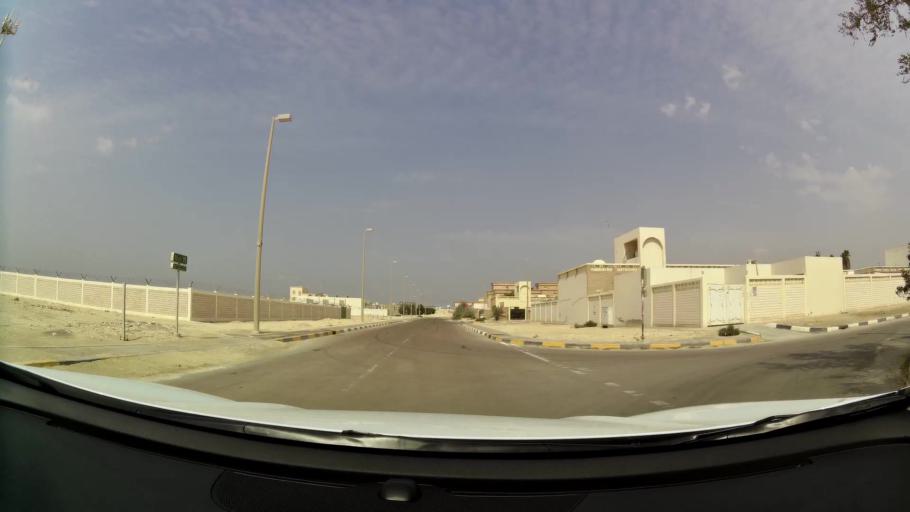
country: AE
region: Abu Dhabi
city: Abu Dhabi
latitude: 24.5252
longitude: 54.6830
